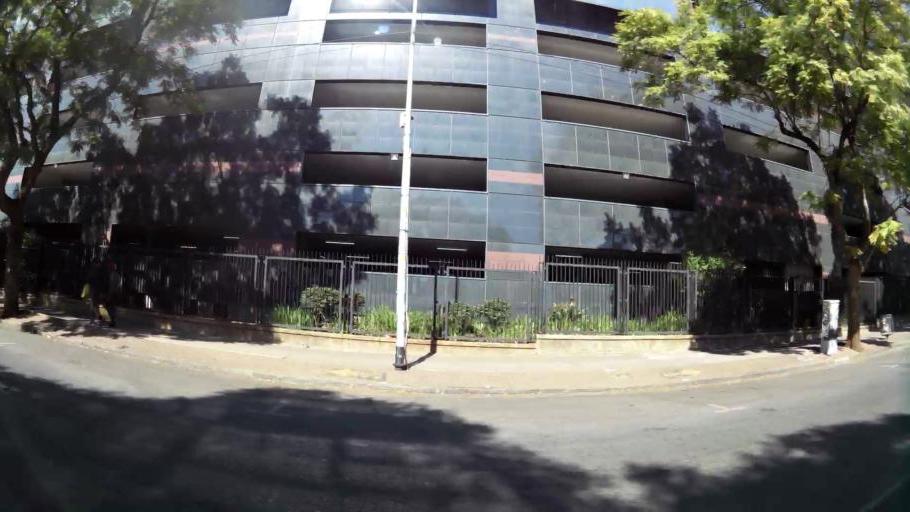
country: ZA
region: Gauteng
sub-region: City of Tshwane Metropolitan Municipality
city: Pretoria
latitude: -25.7444
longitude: 28.1975
